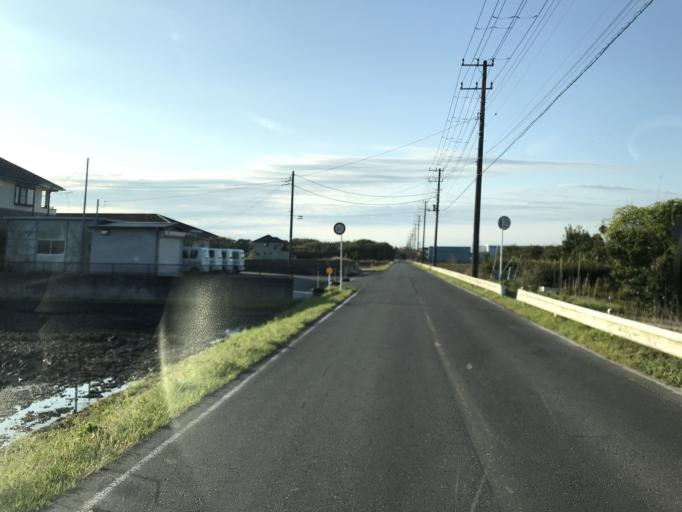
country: JP
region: Chiba
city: Yokaichiba
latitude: 35.6964
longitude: 140.5660
